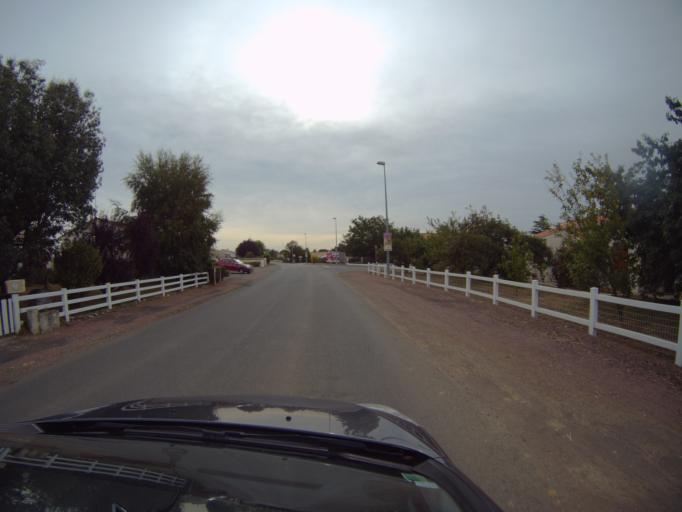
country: FR
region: Pays de la Loire
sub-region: Departement de la Vendee
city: Angles
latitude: 46.4064
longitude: -1.4130
